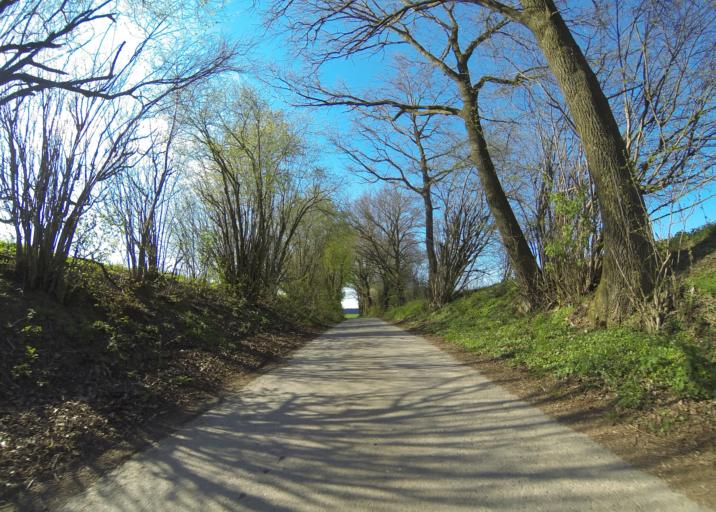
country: DE
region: Baden-Wuerttemberg
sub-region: Tuebingen Region
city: Burgrieden
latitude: 48.2400
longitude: 9.9541
